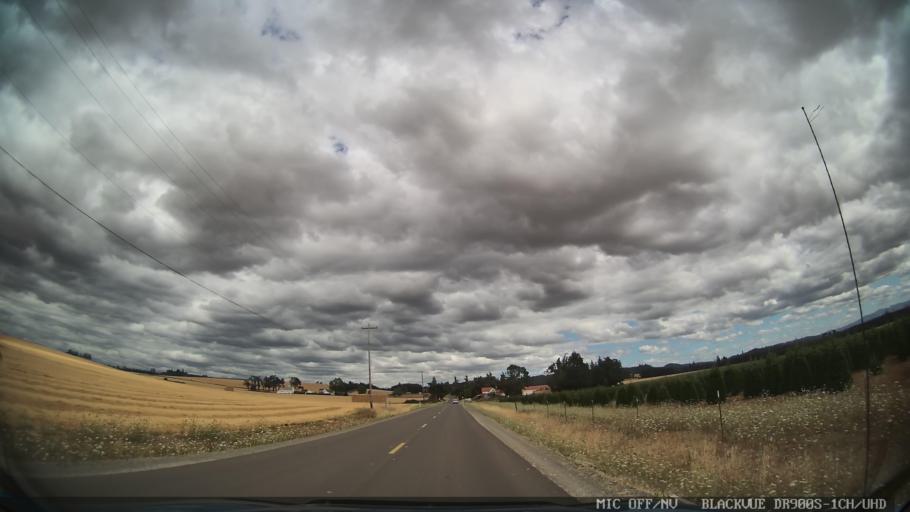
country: US
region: Oregon
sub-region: Marion County
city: Sublimity
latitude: 44.8661
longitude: -122.7626
